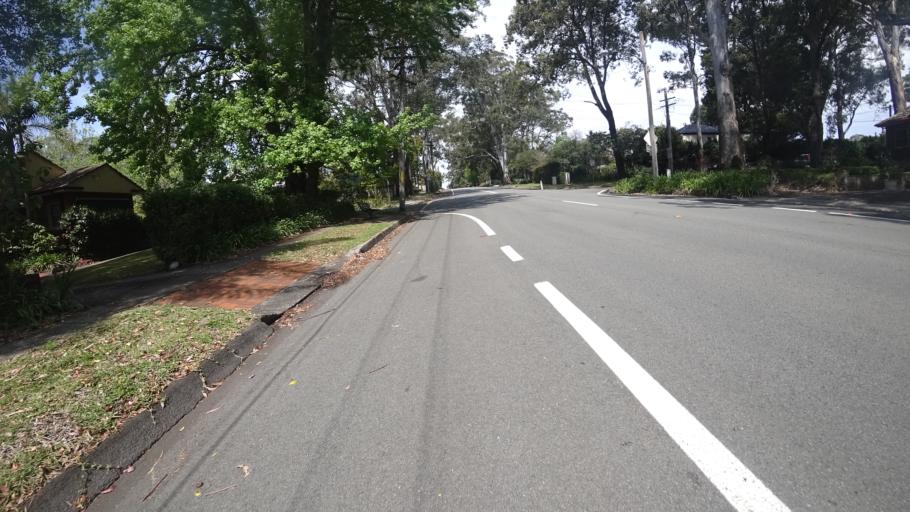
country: AU
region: New South Wales
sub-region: City of Sydney
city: North Turramurra
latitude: -33.7240
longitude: 151.1396
